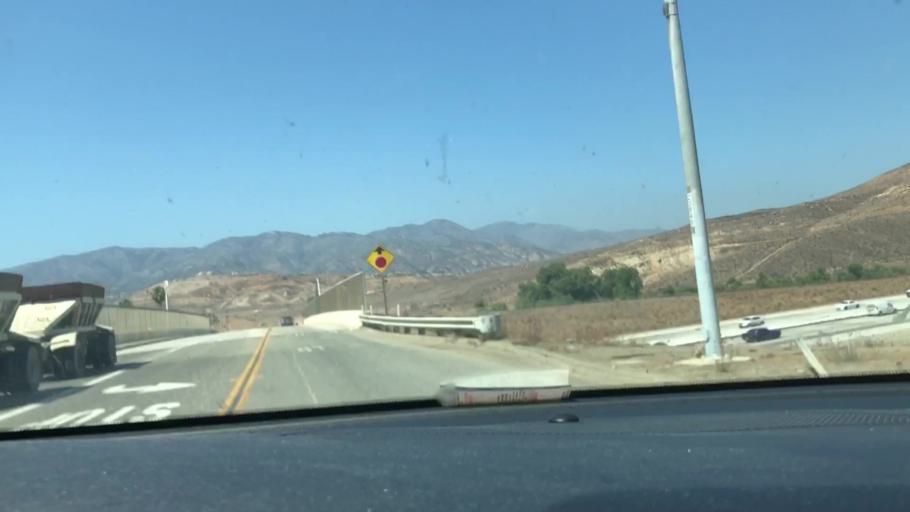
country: US
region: California
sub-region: Riverside County
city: Lake Elsinore
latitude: 33.7070
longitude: -117.3598
